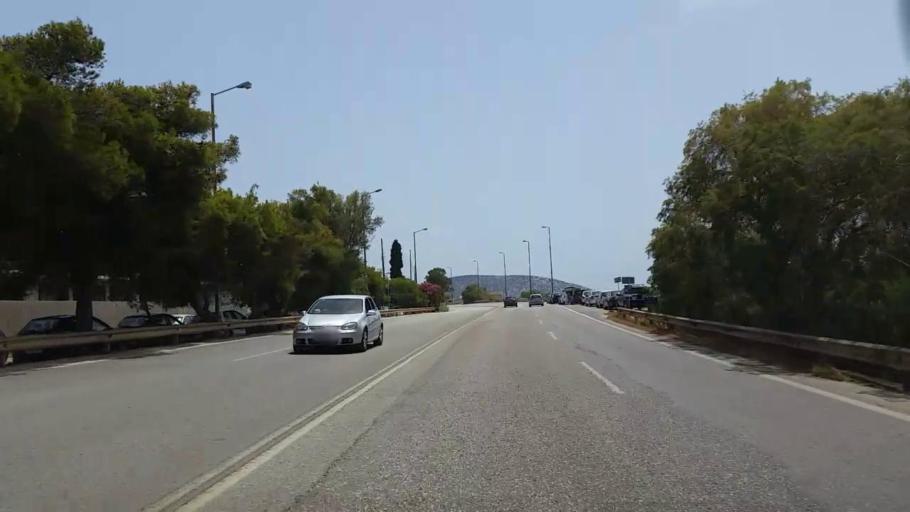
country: GR
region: Attica
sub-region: Nomarchia Anatolikis Attikis
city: Saronida
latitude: 37.7415
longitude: 23.9048
